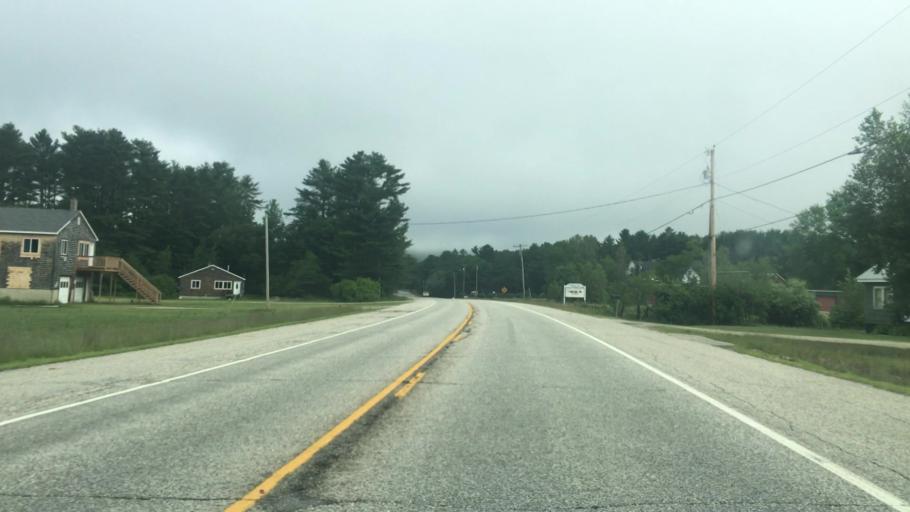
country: US
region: Maine
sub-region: Oxford County
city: Paris
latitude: 44.2773
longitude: -70.5147
